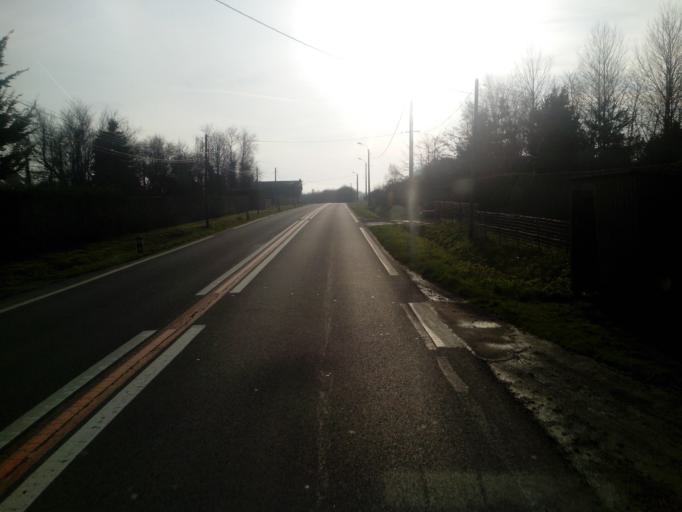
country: FR
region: Brittany
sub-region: Departement d'Ille-et-Vilaine
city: Saint-Meen-le-Grand
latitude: 48.1643
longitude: -2.2106
